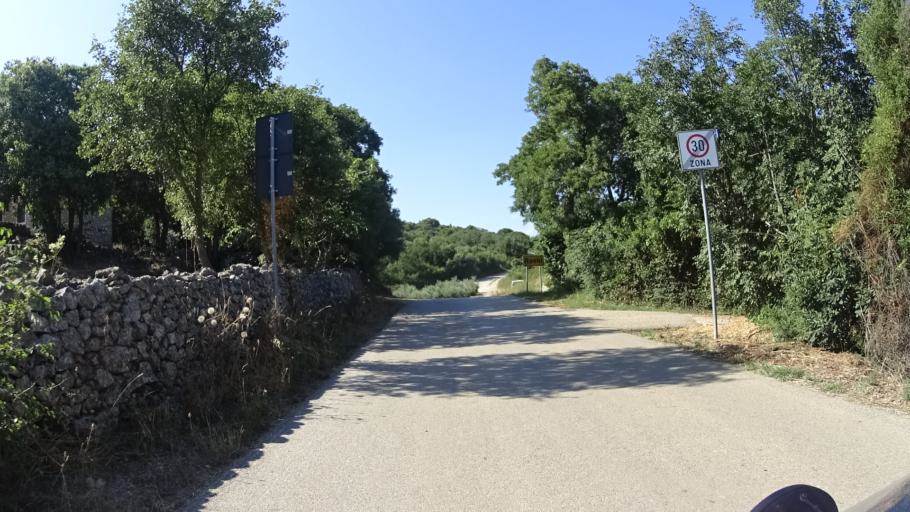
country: HR
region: Istarska
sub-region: Grad Labin
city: Rabac
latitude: 45.0053
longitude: 14.1624
